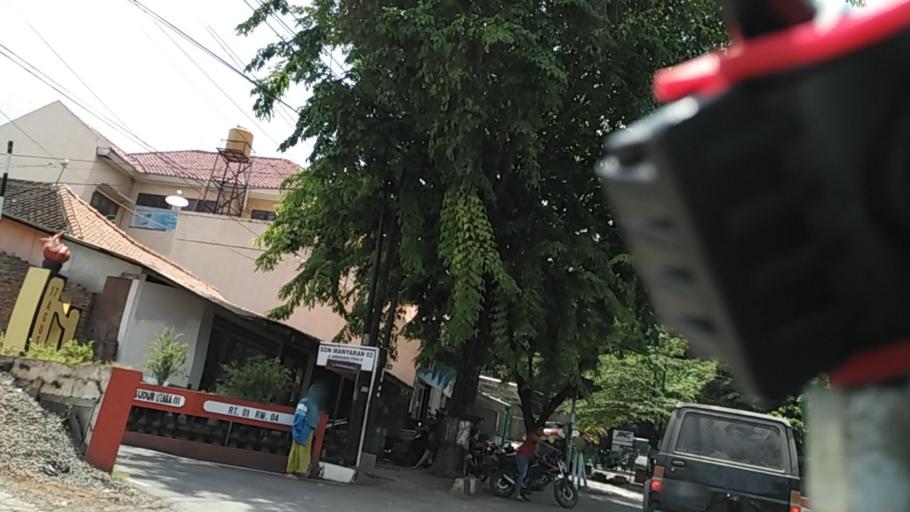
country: ID
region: Central Java
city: Semarang
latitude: -6.9975
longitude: 110.3800
